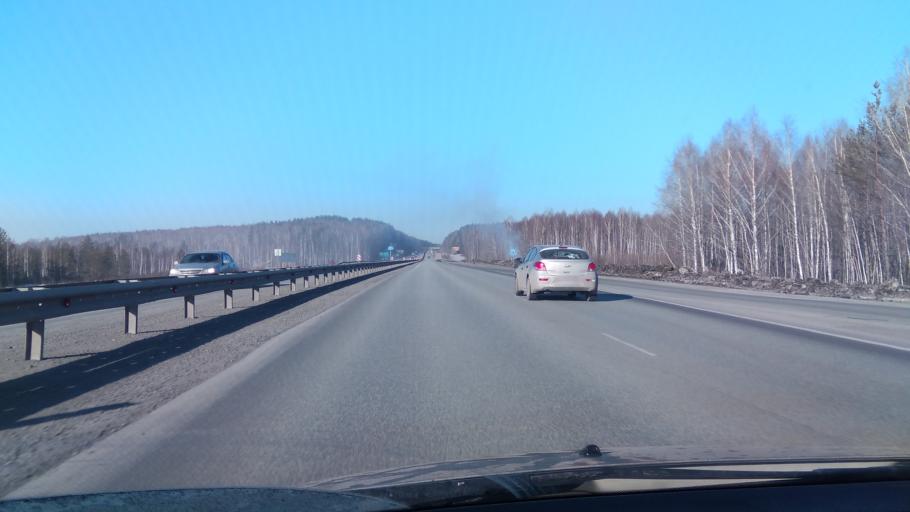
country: RU
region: Sverdlovsk
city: Talitsa
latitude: 56.8377
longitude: 60.1444
